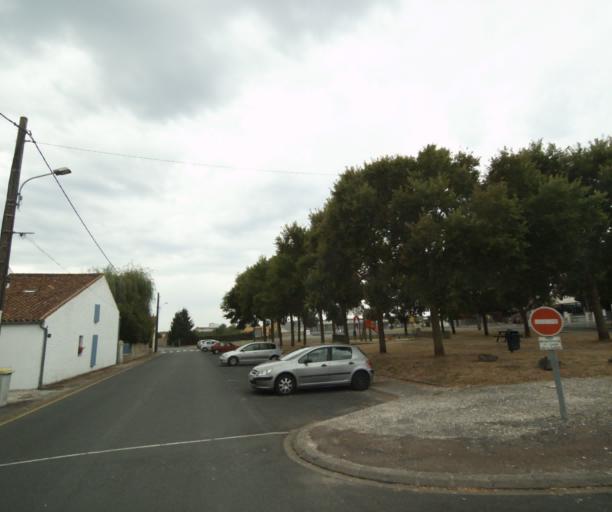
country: FR
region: Poitou-Charentes
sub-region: Departement de la Charente-Maritime
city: Tonnay-Charente
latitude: 45.9474
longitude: -0.8881
